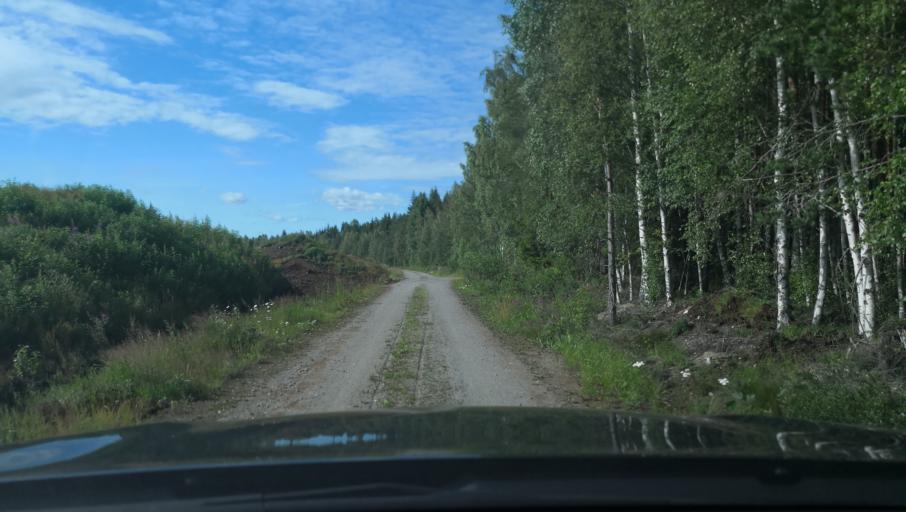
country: SE
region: Vaestmanland
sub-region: Surahammars Kommun
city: Surahammar
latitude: 59.6674
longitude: 16.1048
